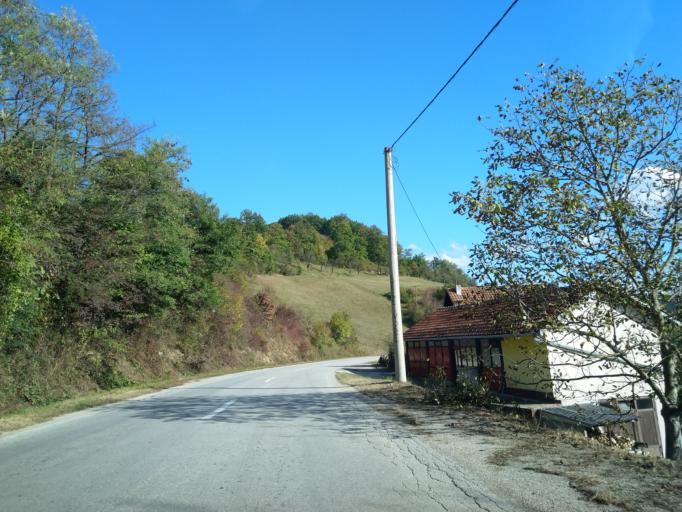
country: RS
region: Central Serbia
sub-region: Zlatiborski Okrug
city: Uzice
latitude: 43.8695
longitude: 19.7997
